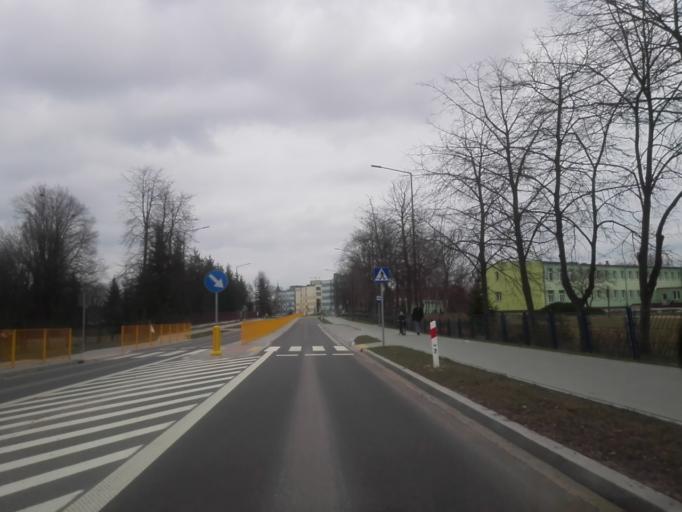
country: PL
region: Podlasie
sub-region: Powiat sejnenski
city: Sejny
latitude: 54.1088
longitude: 23.3380
